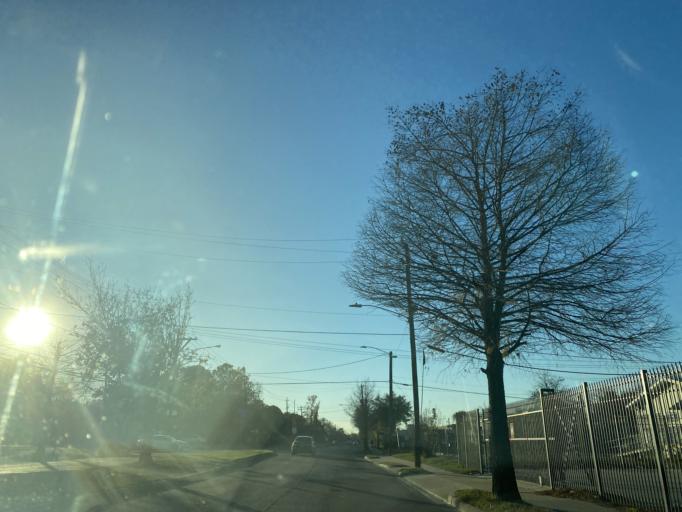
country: US
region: Texas
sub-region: Harris County
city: Houston
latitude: 29.8287
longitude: -95.3876
